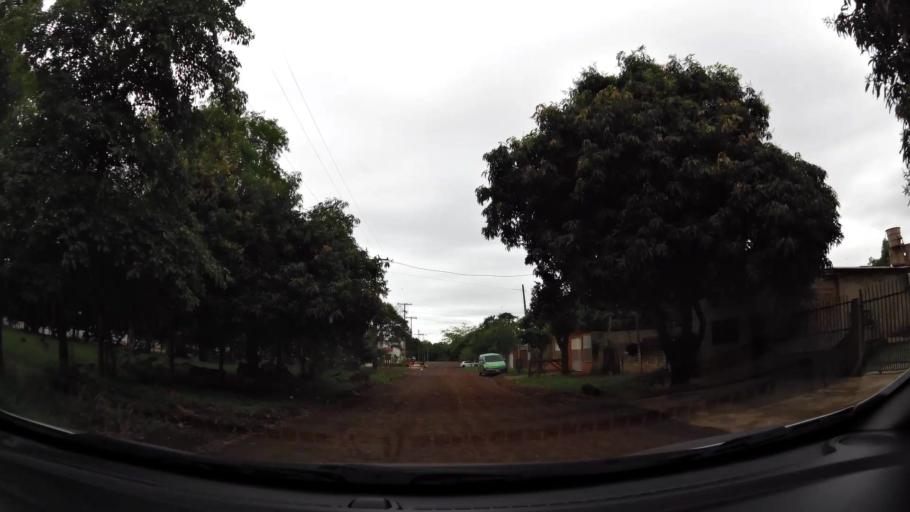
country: PY
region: Alto Parana
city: Ciudad del Este
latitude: -25.4370
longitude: -54.6376
